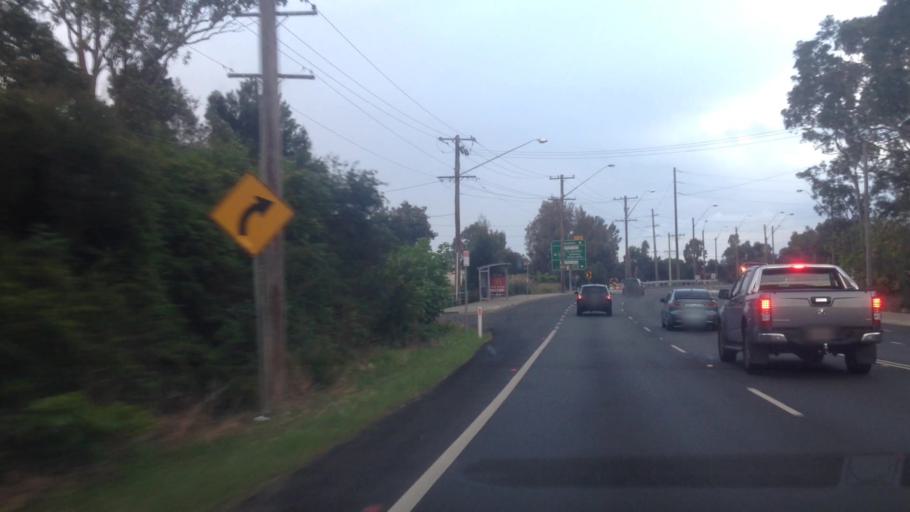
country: AU
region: New South Wales
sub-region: Wyong Shire
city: Kanwal
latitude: -33.2536
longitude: 151.4880
